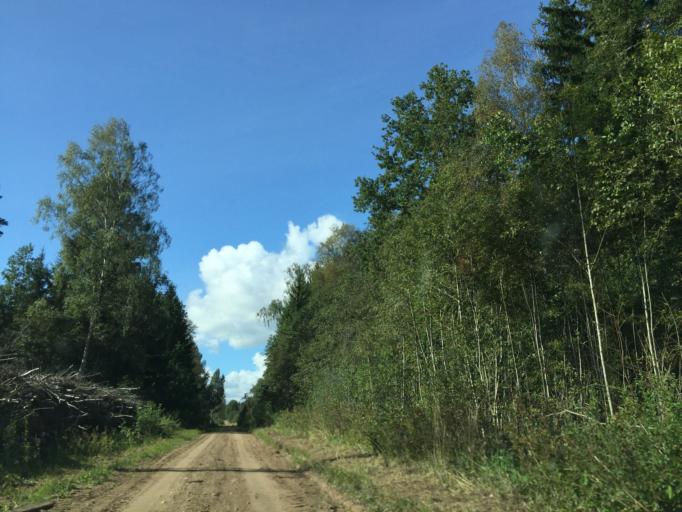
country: LV
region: Kuldigas Rajons
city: Kuldiga
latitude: 56.9937
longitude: 21.8333
